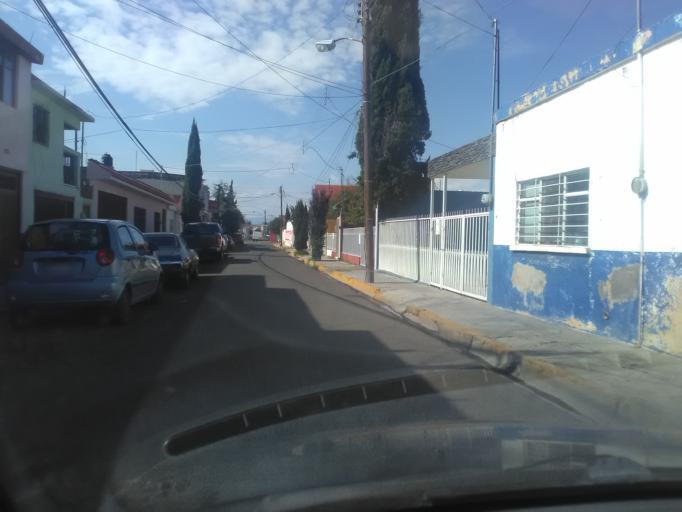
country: MX
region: Durango
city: Victoria de Durango
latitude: 24.0220
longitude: -104.6576
